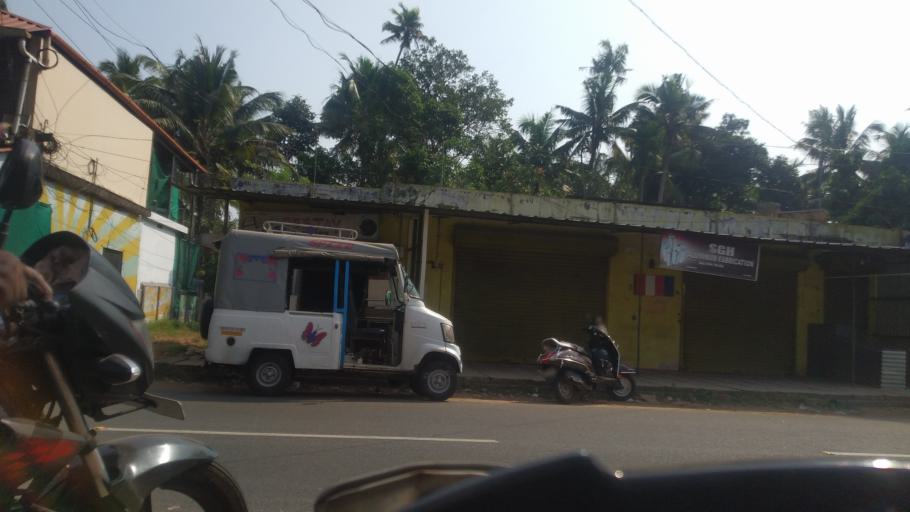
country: IN
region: Kerala
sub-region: Thrissur District
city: Kodungallur
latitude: 10.2122
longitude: 76.1886
